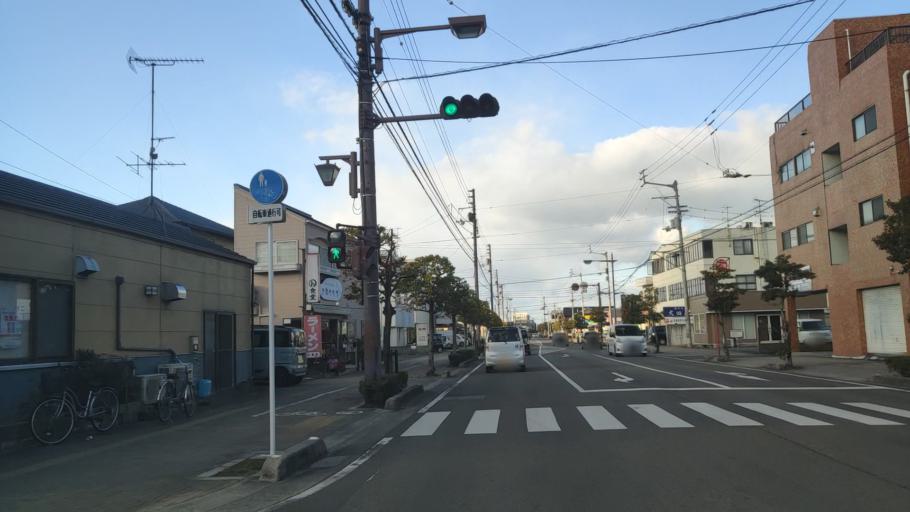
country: JP
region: Ehime
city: Saijo
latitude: 33.9195
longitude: 133.1851
